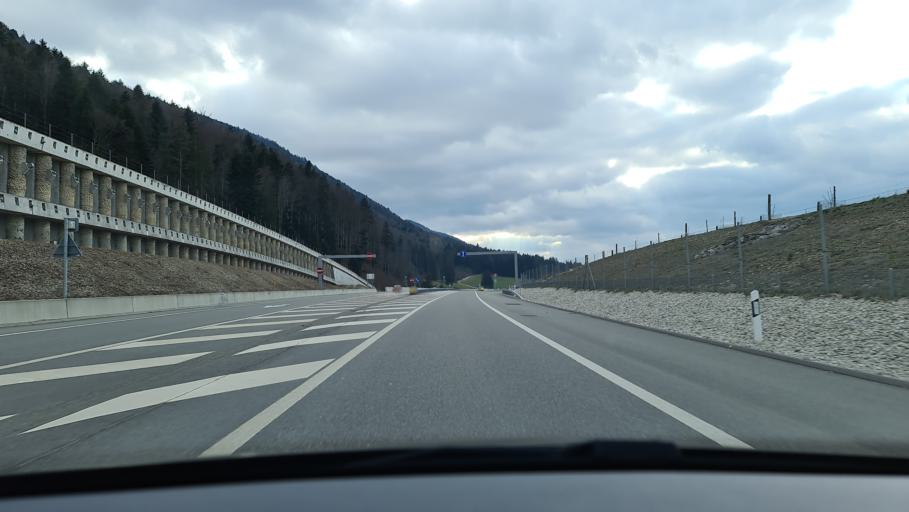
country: CH
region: Bern
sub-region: Jura bernois
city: Court
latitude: 47.2340
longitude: 7.3389
